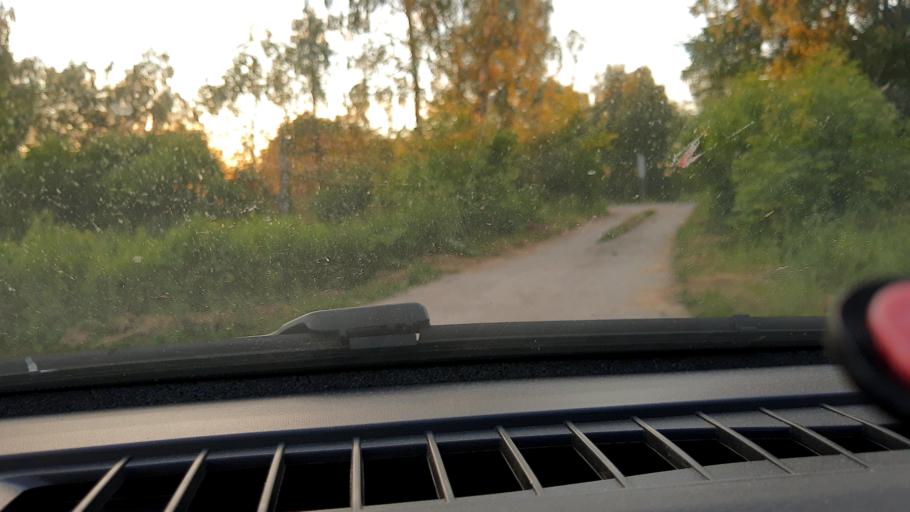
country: RU
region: Nizjnij Novgorod
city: Afonino
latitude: 56.3172
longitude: 44.2024
